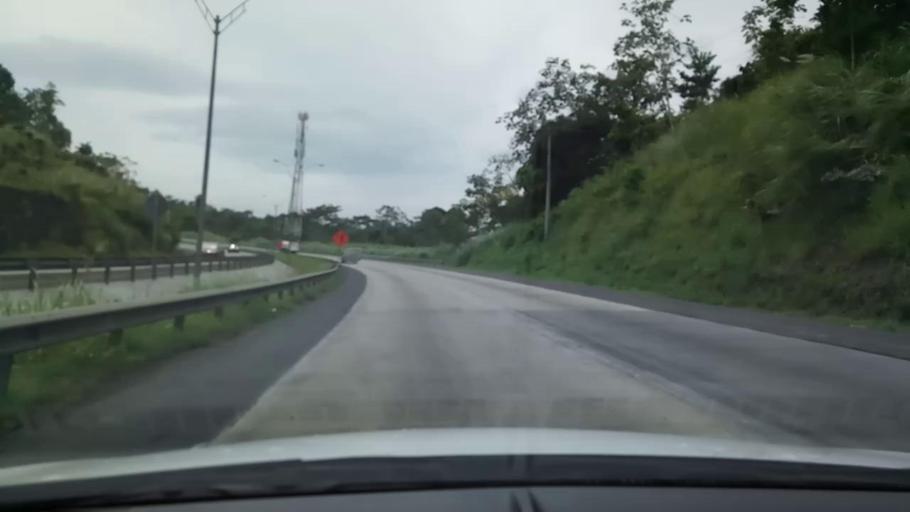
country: PA
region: Panama
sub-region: Distrito de Panama
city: Paraiso
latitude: 8.9992
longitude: -79.6523
